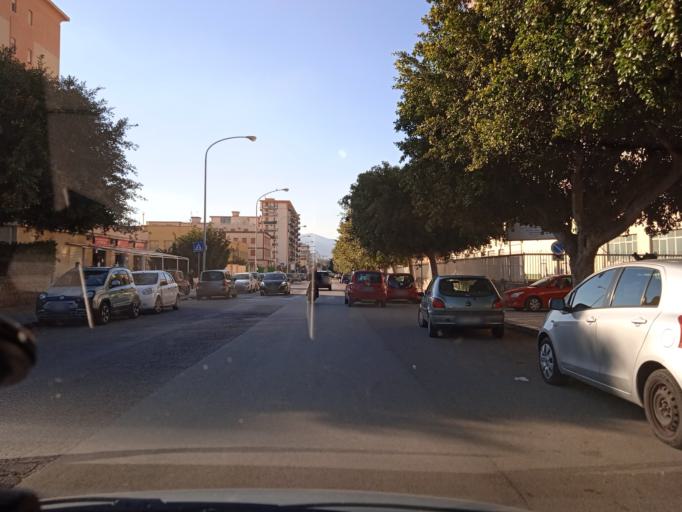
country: IT
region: Sicily
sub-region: Palermo
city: Ciaculli
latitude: 38.1036
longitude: 13.3851
